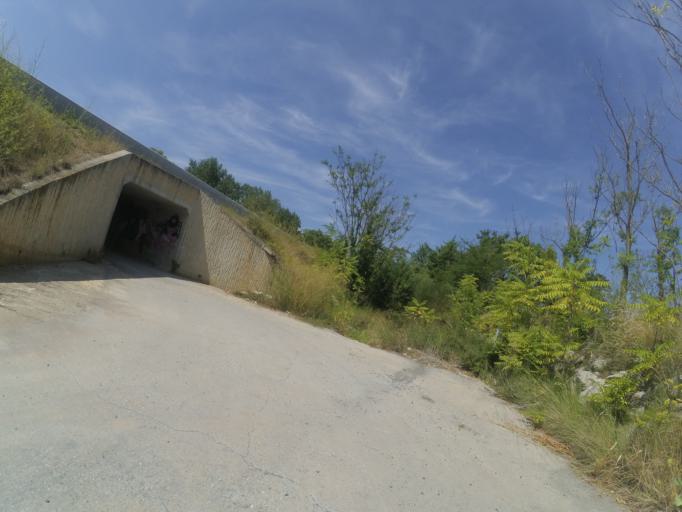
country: FR
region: Languedoc-Roussillon
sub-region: Departement des Pyrenees-Orientales
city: Peyrestortes
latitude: 42.7582
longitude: 2.8559
